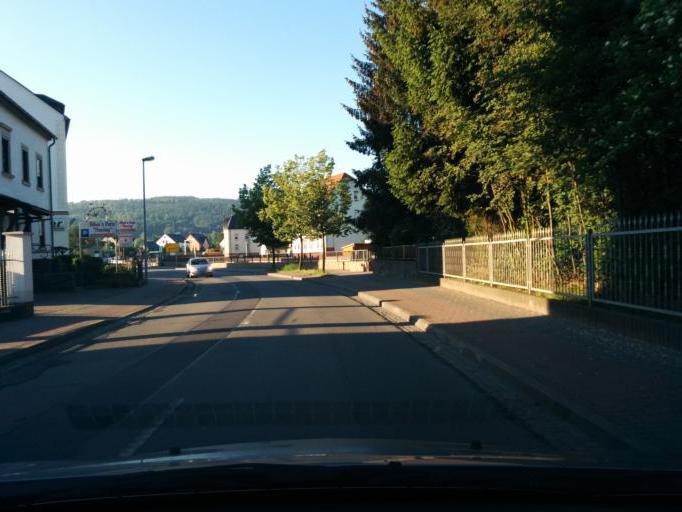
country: DE
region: Saxony
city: Floha
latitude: 50.8477
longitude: 13.0790
